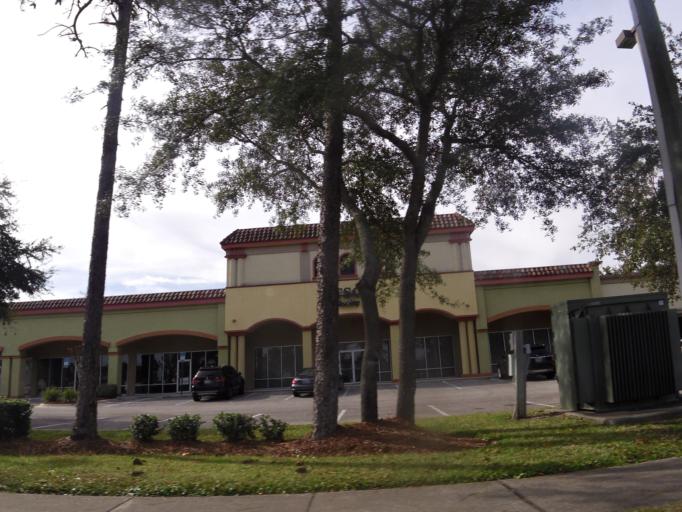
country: US
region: Florida
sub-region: Saint Johns County
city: Fruit Cove
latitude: 30.2230
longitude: -81.5929
